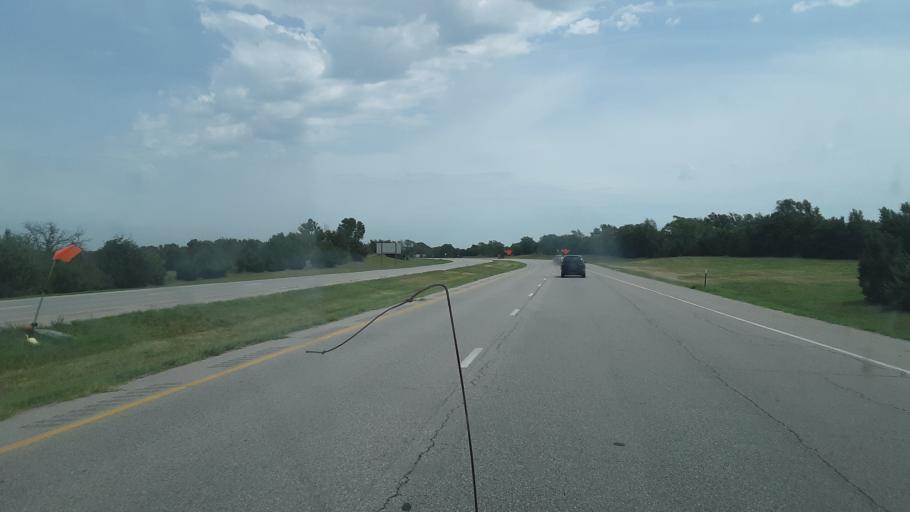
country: US
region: Kansas
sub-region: Sedgwick County
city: Bellaire
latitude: 37.7702
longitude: -97.2964
